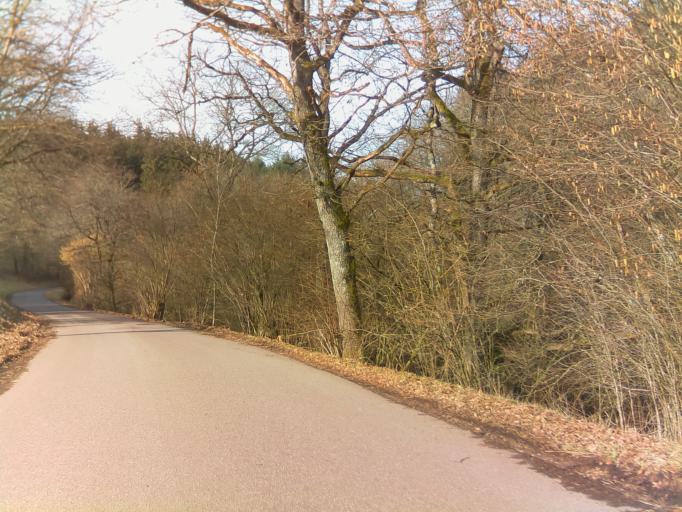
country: DE
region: Rheinland-Pfalz
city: Hahnweiler
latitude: 49.5358
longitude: 7.2114
